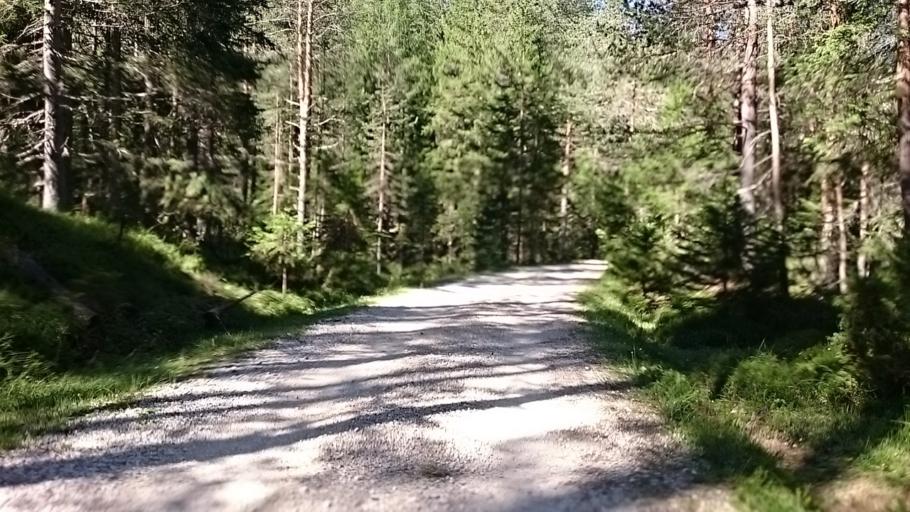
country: IT
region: Veneto
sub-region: Provincia di Belluno
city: Cortina d'Ampezzo
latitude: 46.6178
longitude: 12.2065
